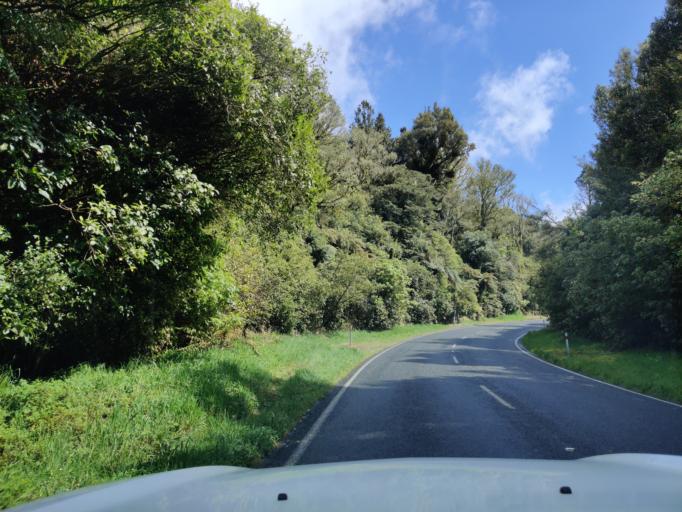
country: NZ
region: Bay of Plenty
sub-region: Rotorua District
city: Rotorua
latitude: -38.1825
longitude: 176.3275
